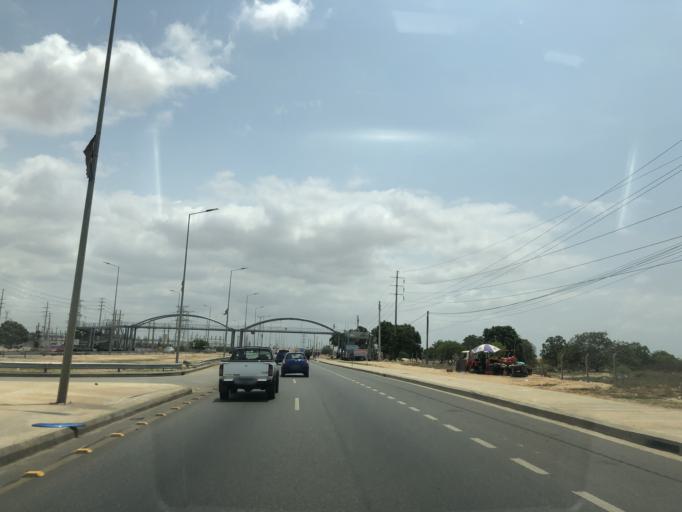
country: AO
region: Luanda
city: Luanda
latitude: -8.9656
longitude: 13.2556
